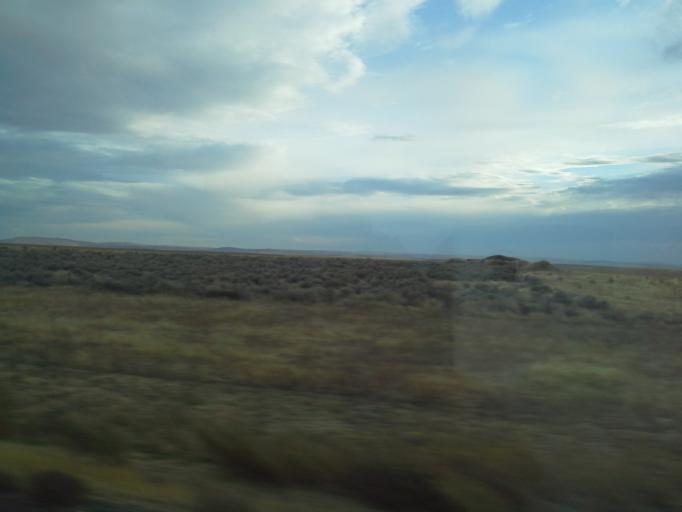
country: US
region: Oregon
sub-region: Umatilla County
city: Stanfield
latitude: 45.7221
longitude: -119.0255
